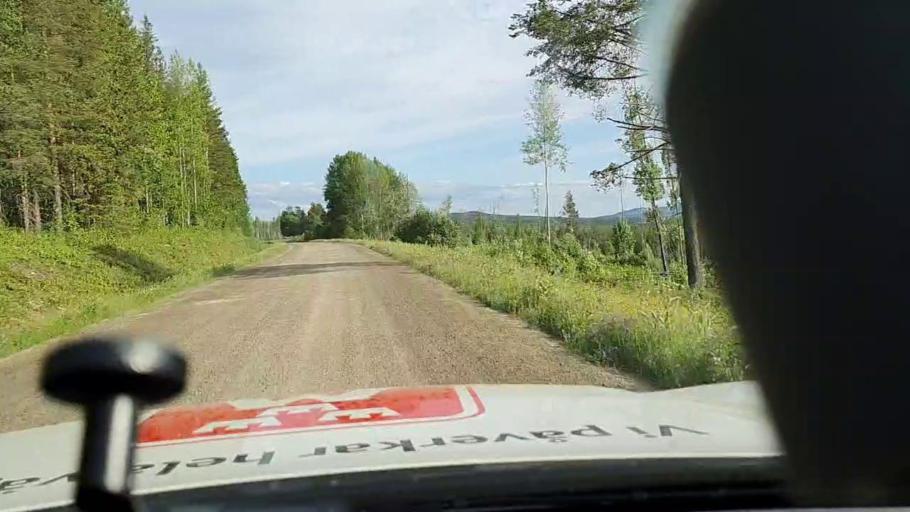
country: SE
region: Norrbotten
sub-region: Alvsbyns Kommun
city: AElvsbyn
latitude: 66.1901
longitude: 21.1978
